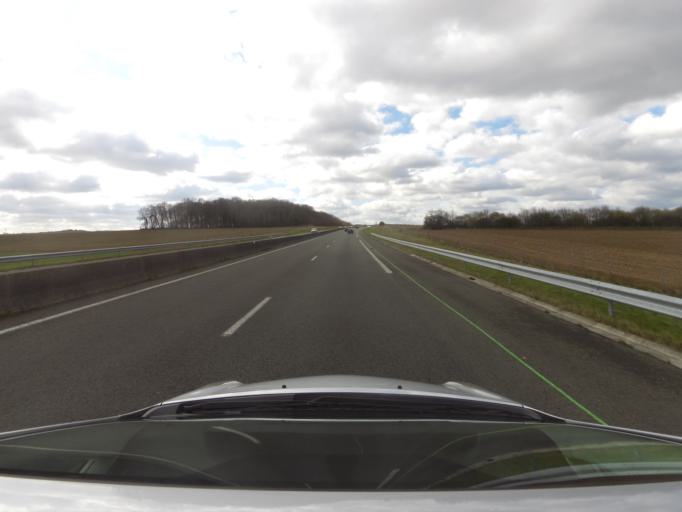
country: FR
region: Picardie
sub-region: Departement de la Somme
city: Sailly-Flibeaucourt
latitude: 50.1920
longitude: 1.7579
